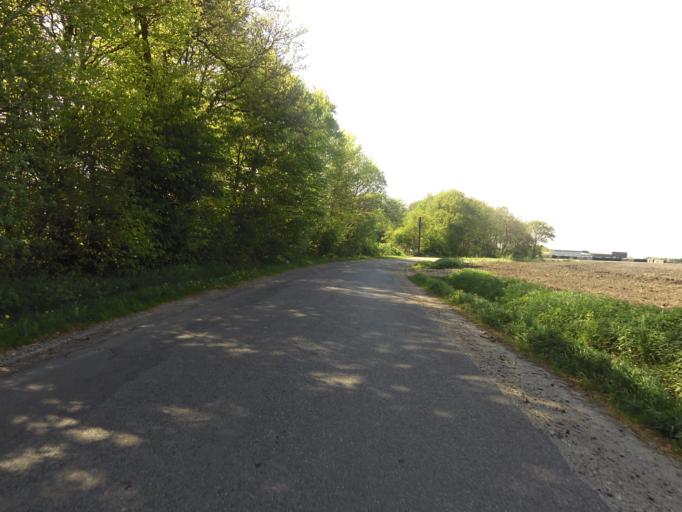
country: DK
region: South Denmark
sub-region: Tonder Kommune
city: Sherrebek
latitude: 55.2205
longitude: 8.8385
